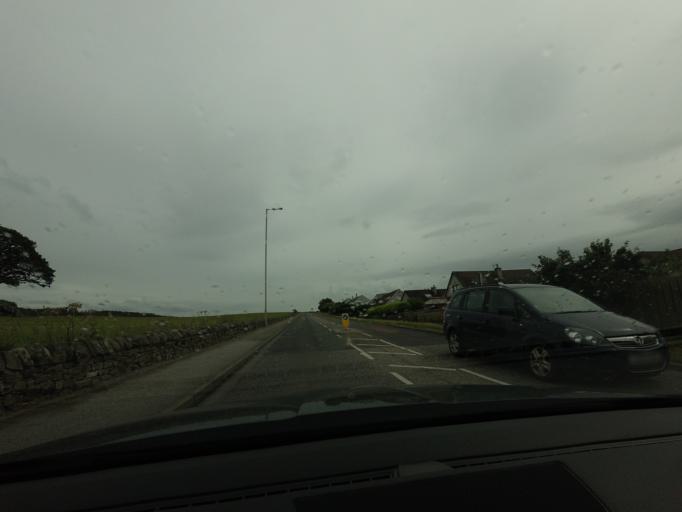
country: GB
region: Scotland
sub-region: Moray
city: Cullen
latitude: 57.6883
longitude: -2.8156
